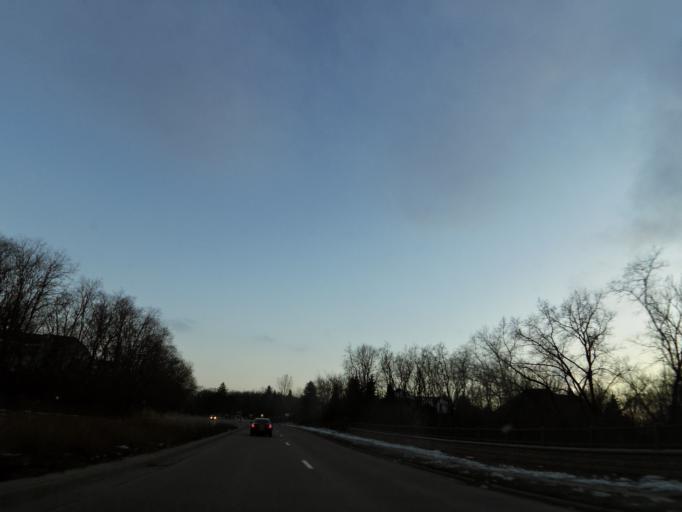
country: US
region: Minnesota
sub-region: Hennepin County
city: Minnetonka Mills
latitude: 44.9045
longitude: -93.4275
